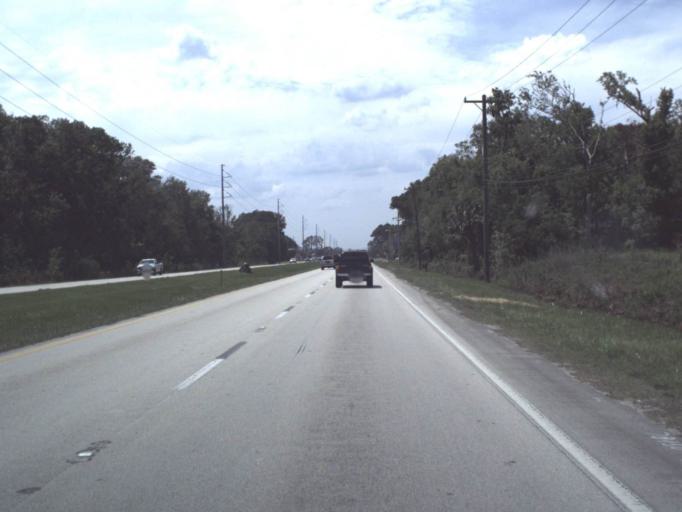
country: US
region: Florida
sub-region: Duval County
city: Jacksonville
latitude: 30.2517
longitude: -81.6065
